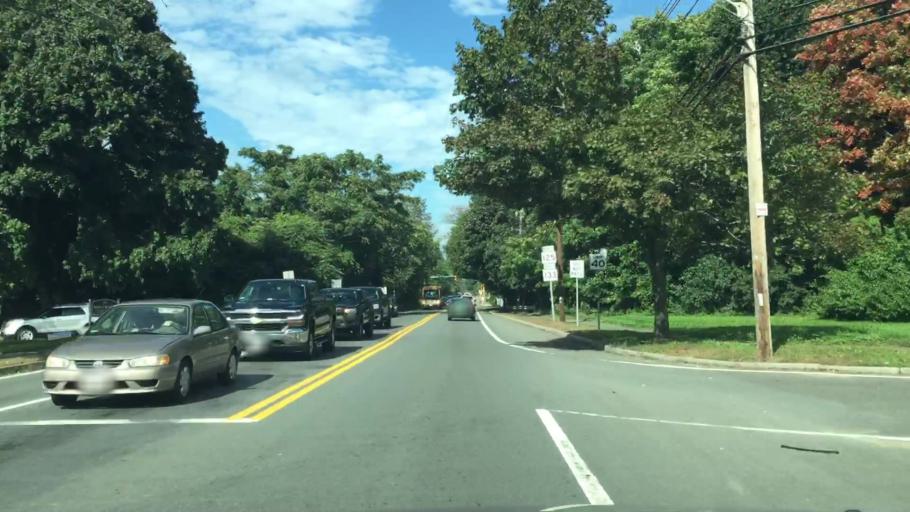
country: US
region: Massachusetts
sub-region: Essex County
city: Andover
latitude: 42.6772
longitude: -71.1249
